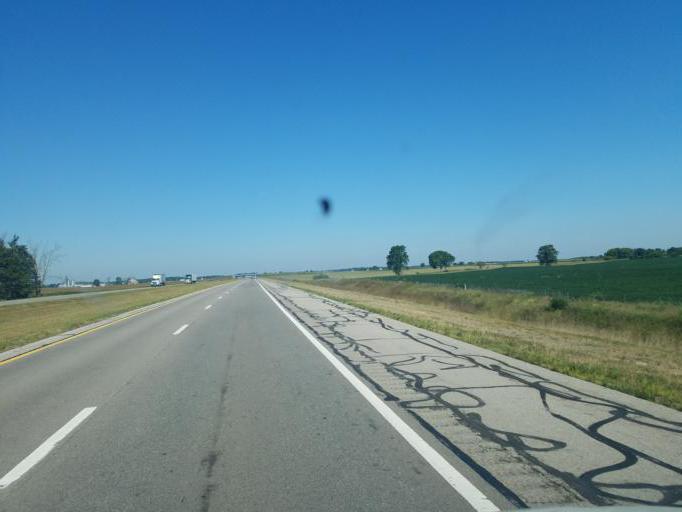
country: US
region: Ohio
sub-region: Crawford County
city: Bucyrus
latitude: 40.7761
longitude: -82.8893
